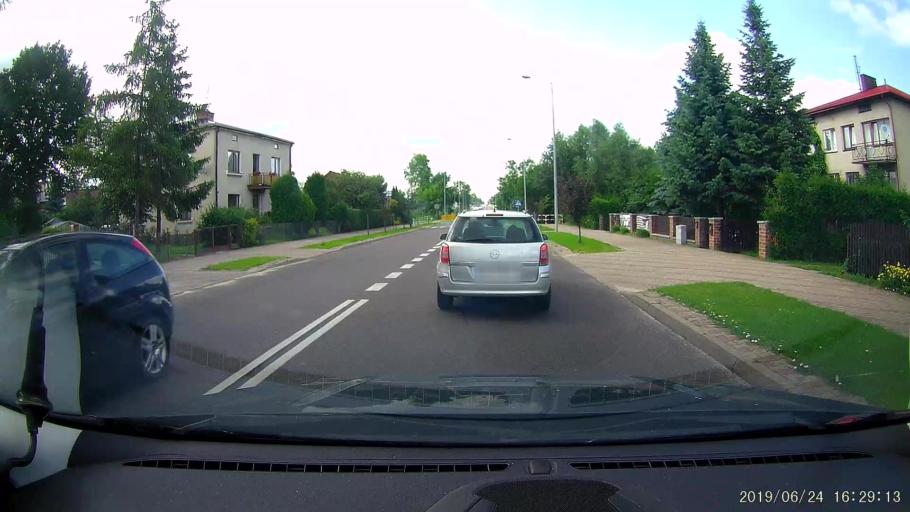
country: PL
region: Lublin Voivodeship
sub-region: Powiat tomaszowski
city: Tomaszow Lubelski
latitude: 50.4578
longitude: 23.4212
